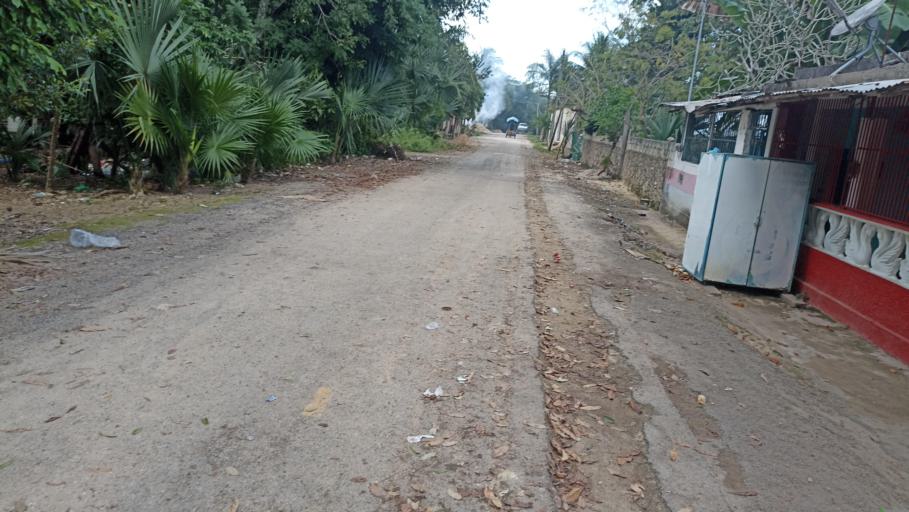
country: MX
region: Quintana Roo
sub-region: Felipe Carrillo Puerto
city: X-Hazil Sur
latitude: 19.4160
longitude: -88.0494
